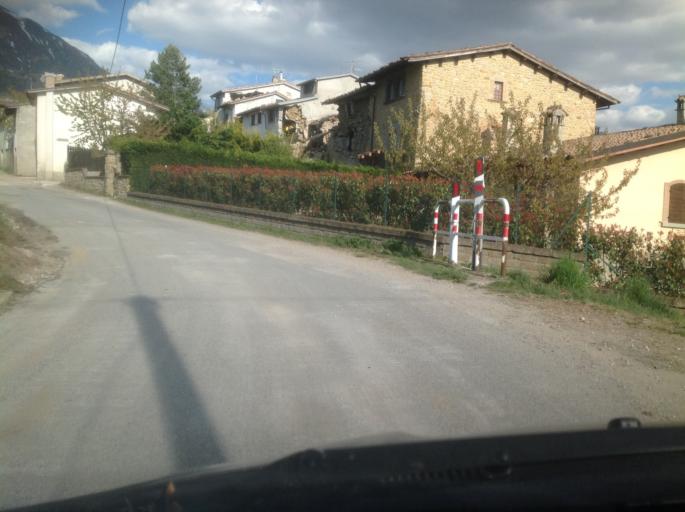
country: IT
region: Latium
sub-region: Provincia di Rieti
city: Amatrice
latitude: 42.6342
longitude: 13.3024
